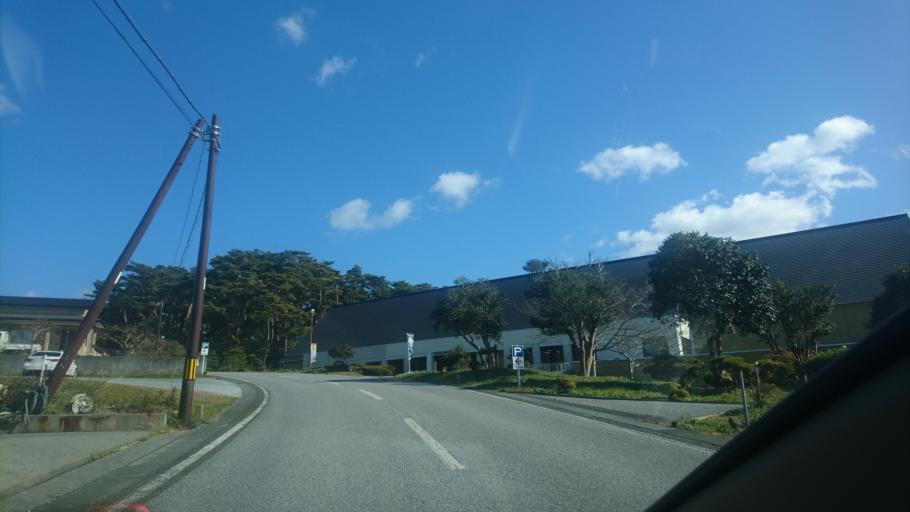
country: JP
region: Iwate
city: Ofunato
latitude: 38.9889
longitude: 141.7409
